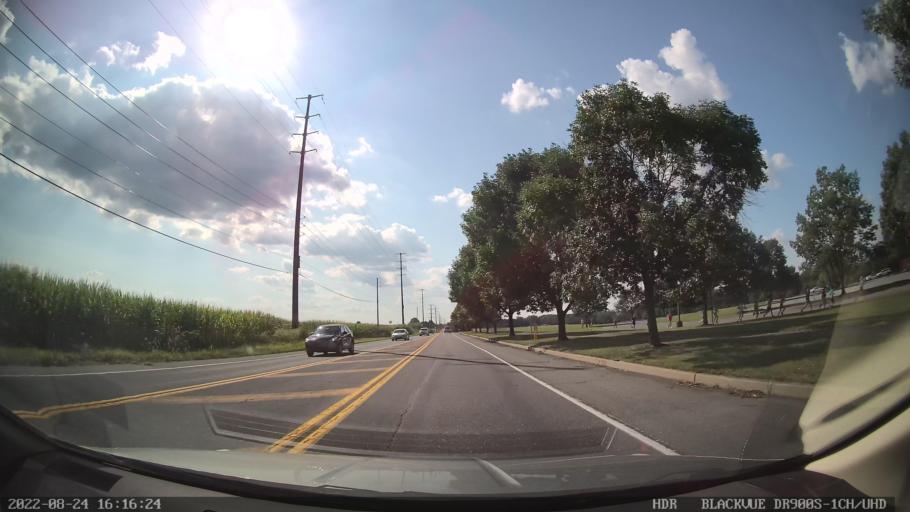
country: US
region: Pennsylvania
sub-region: Lehigh County
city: Ancient Oaks
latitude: 40.5476
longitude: -75.5725
